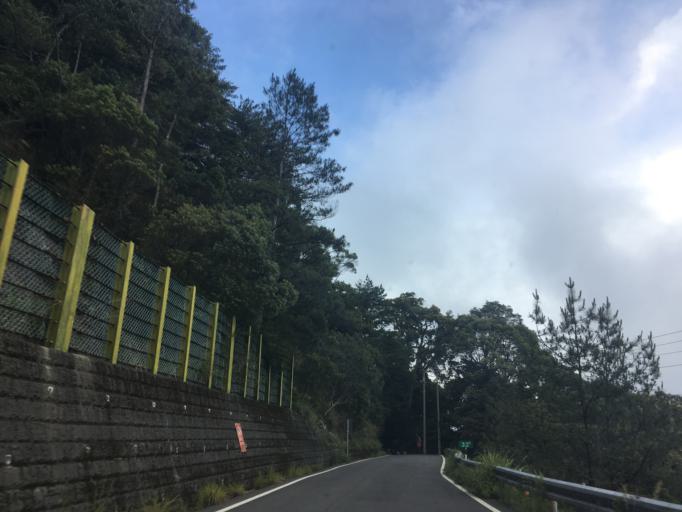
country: TW
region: Taiwan
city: Fengyuan
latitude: 24.2334
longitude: 120.9804
